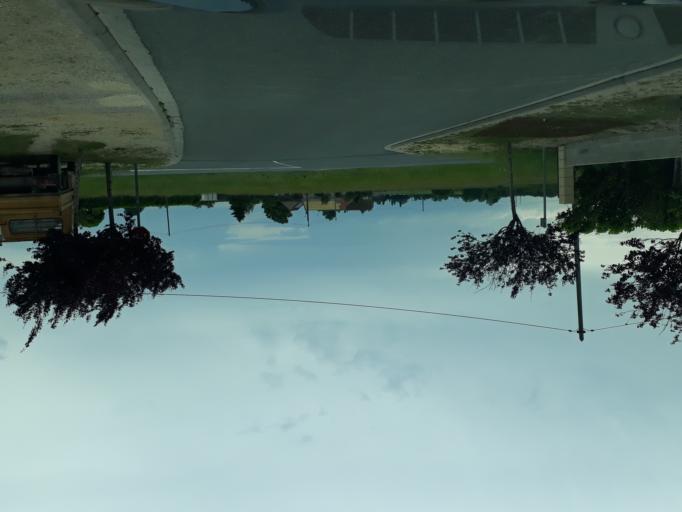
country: FR
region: Centre
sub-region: Departement du Loiret
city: Saint-Pere-sur-Loire
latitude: 47.7606
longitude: 2.3571
